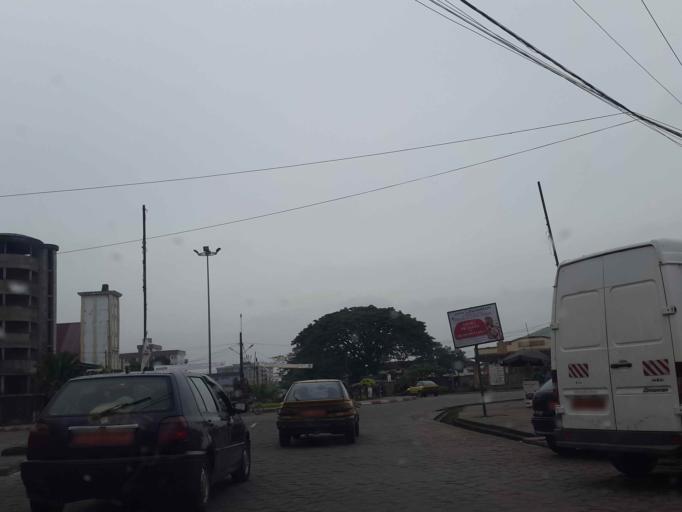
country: CM
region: Littoral
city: Douala
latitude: 4.0500
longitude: 9.7020
